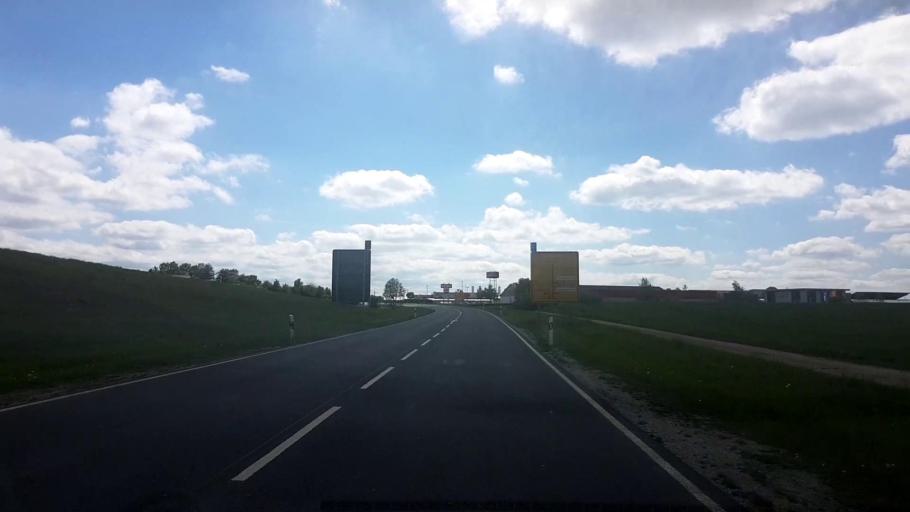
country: DE
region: Bavaria
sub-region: Upper Franconia
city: Untersiemau
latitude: 50.1996
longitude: 10.9676
